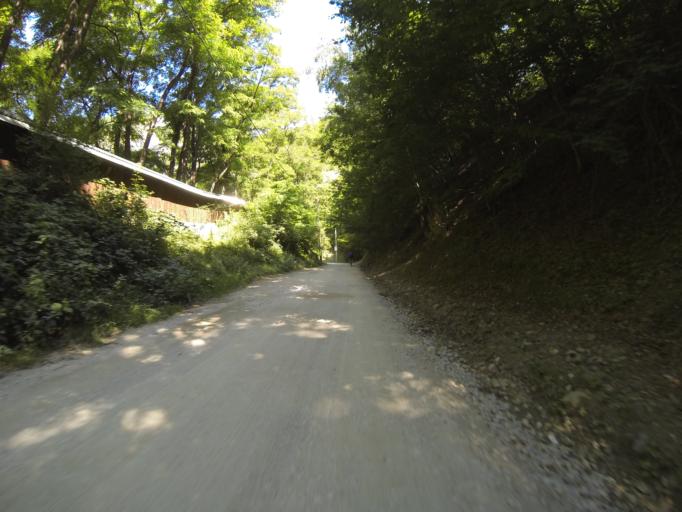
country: RO
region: Gorj
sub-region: Comuna Polovragi
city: Polovragi
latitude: 45.1965
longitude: 23.7878
